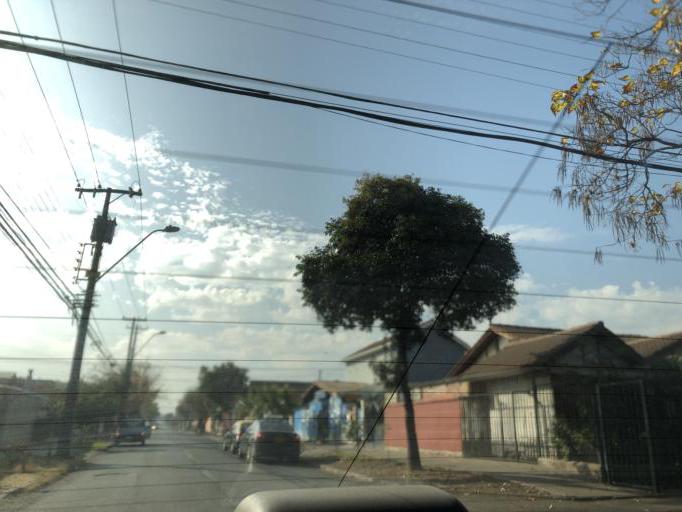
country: CL
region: Santiago Metropolitan
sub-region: Provincia de Cordillera
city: Puente Alto
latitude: -33.5920
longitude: -70.5764
